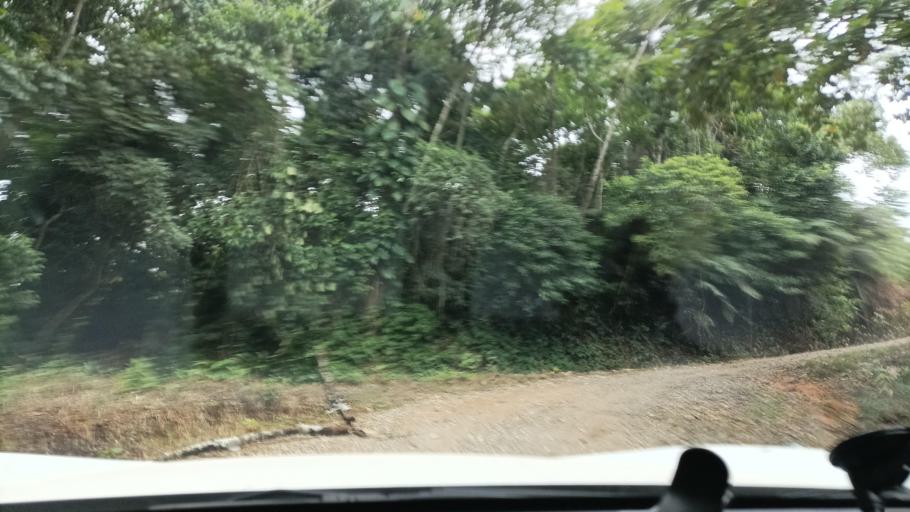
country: MX
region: Veracruz
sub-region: Uxpanapa
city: Poblado 10
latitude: 17.4393
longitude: -94.4120
